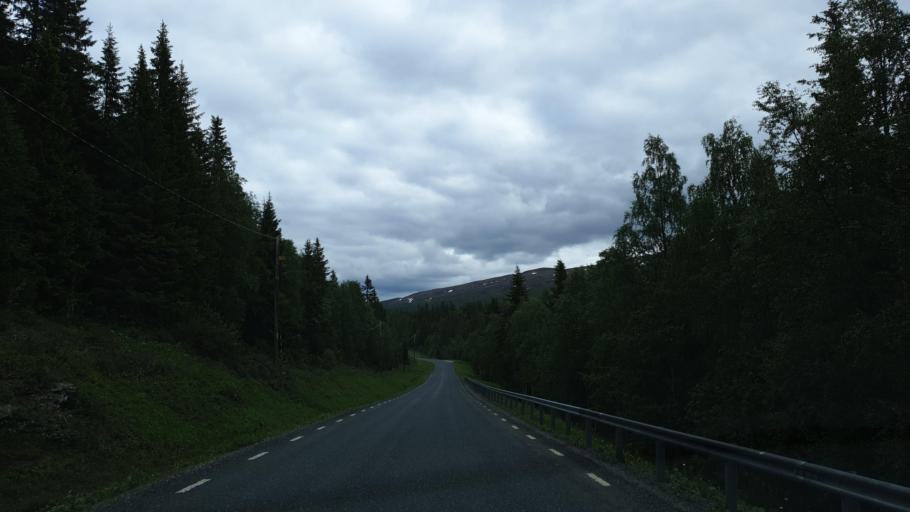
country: NO
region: Nordland
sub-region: Hattfjelldal
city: Hattfjelldal
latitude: 65.4343
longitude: 14.5795
